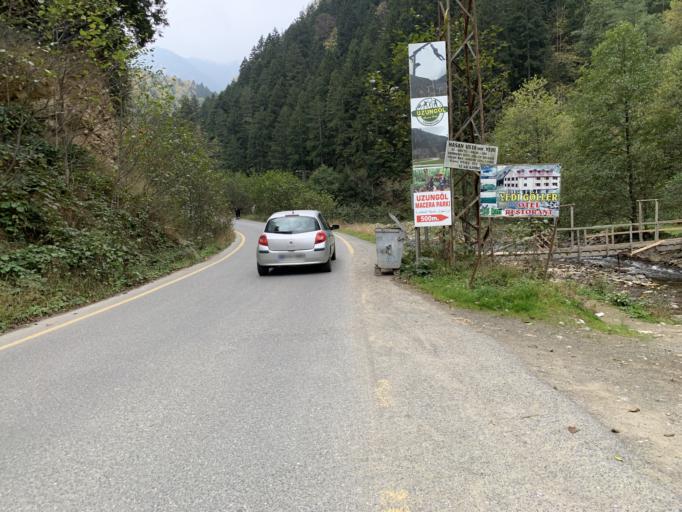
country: TR
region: Trabzon
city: Uzungol
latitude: 40.6006
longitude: 40.3172
